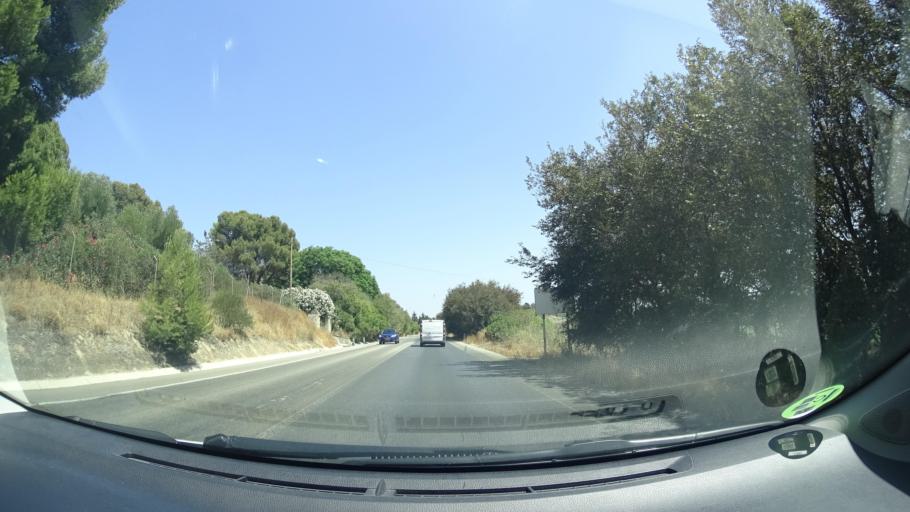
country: ES
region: Andalusia
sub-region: Provincia de Cadiz
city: Jerez de la Frontera
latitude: 36.6572
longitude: -6.0965
